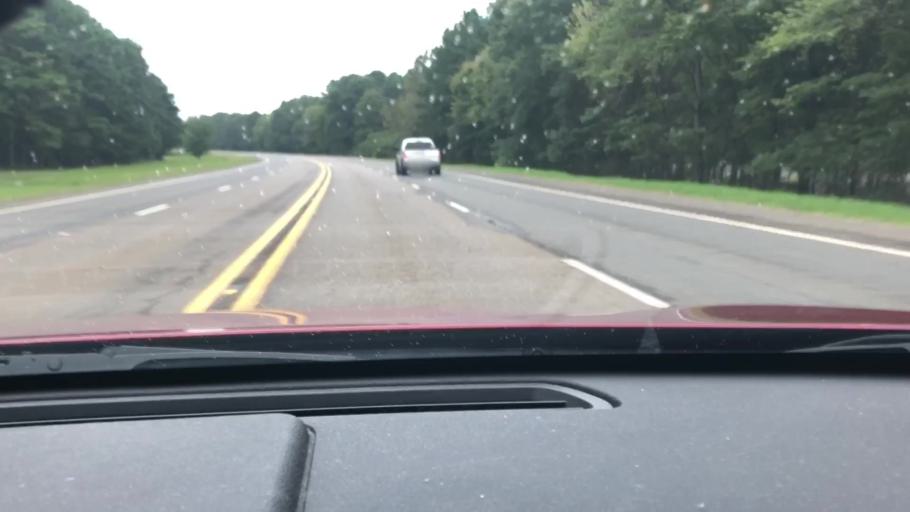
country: US
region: Arkansas
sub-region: Lafayette County
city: Lewisville
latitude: 33.3551
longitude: -93.5691
